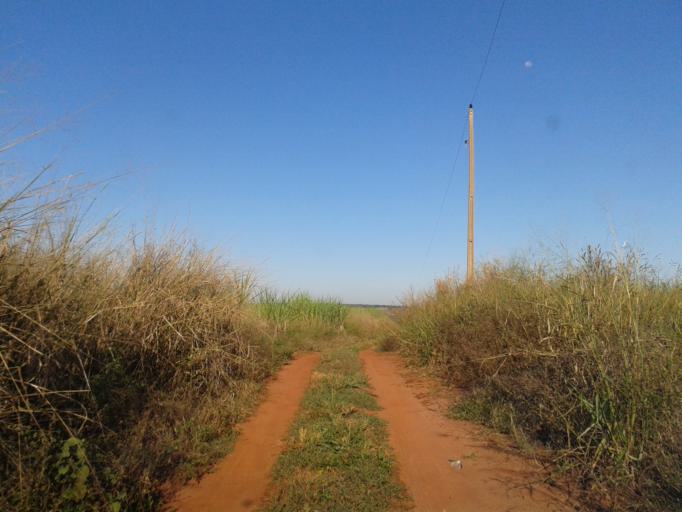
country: BR
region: Minas Gerais
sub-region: Santa Vitoria
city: Santa Vitoria
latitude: -19.0209
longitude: -50.3612
